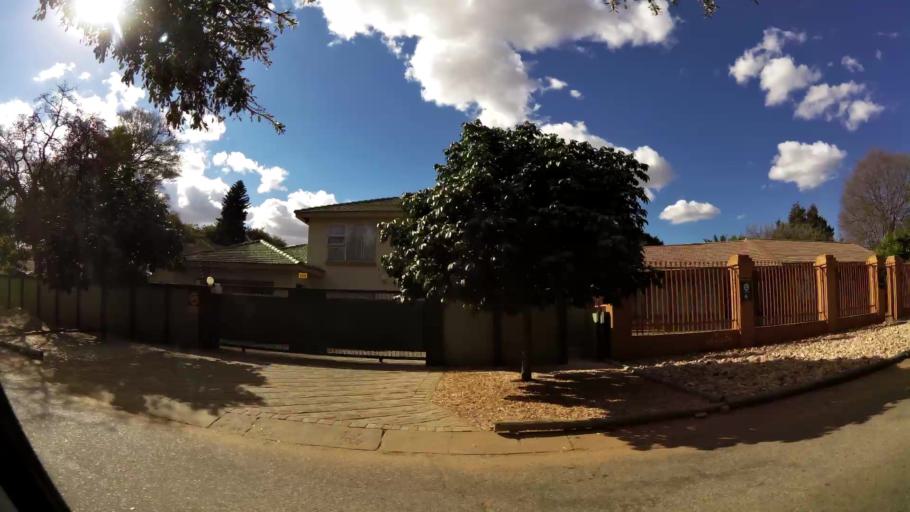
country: ZA
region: Limpopo
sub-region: Capricorn District Municipality
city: Polokwane
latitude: -23.8914
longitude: 29.4689
